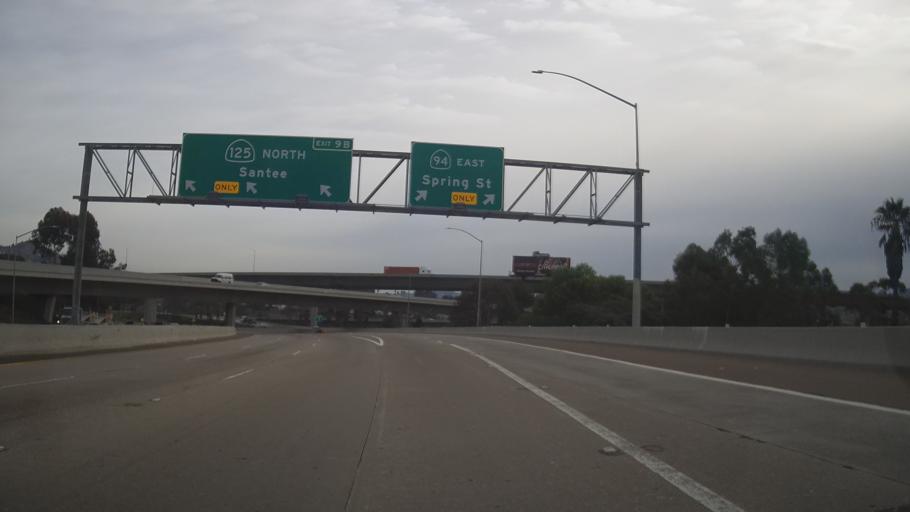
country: US
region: California
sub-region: San Diego County
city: Lemon Grove
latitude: 32.7478
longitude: -117.0253
